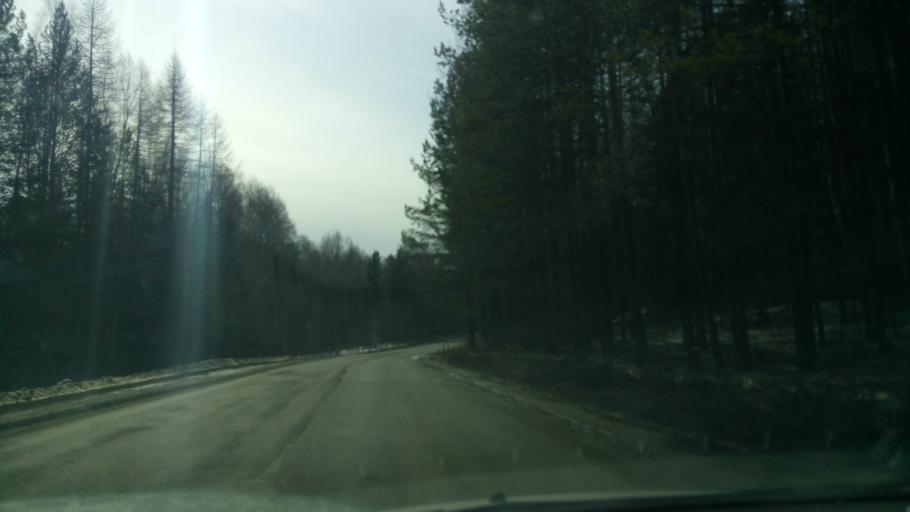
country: RU
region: Sverdlovsk
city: Chernoistochinsk
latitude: 57.7132
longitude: 59.7832
